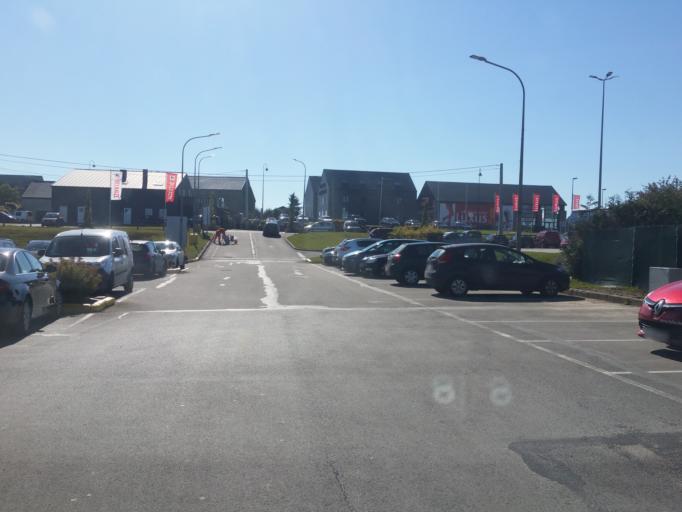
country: BE
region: Wallonia
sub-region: Province du Luxembourg
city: Neufchateau
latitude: 49.9125
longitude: 5.3558
